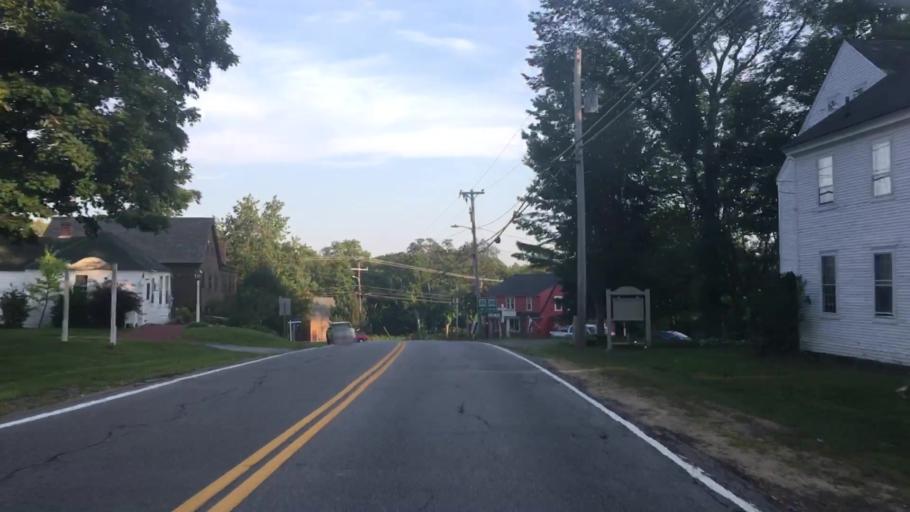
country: US
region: New Hampshire
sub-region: Belknap County
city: Gilmanton
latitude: 43.4249
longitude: -71.4141
